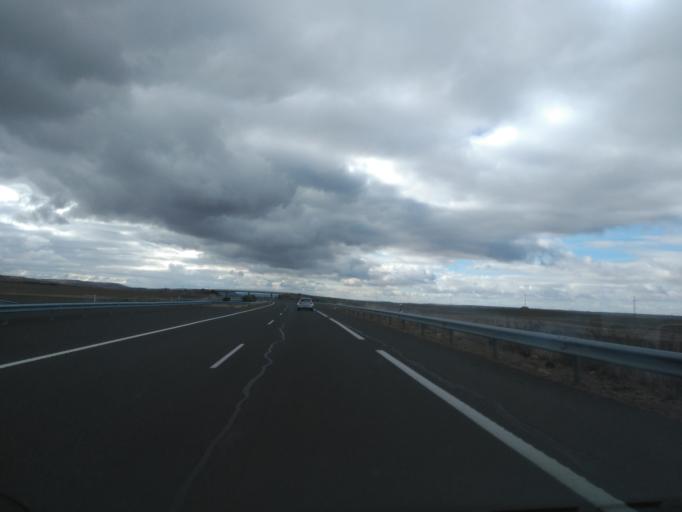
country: ES
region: Castille and Leon
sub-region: Provincia de Palencia
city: Amusco
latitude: 42.1670
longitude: -4.4611
